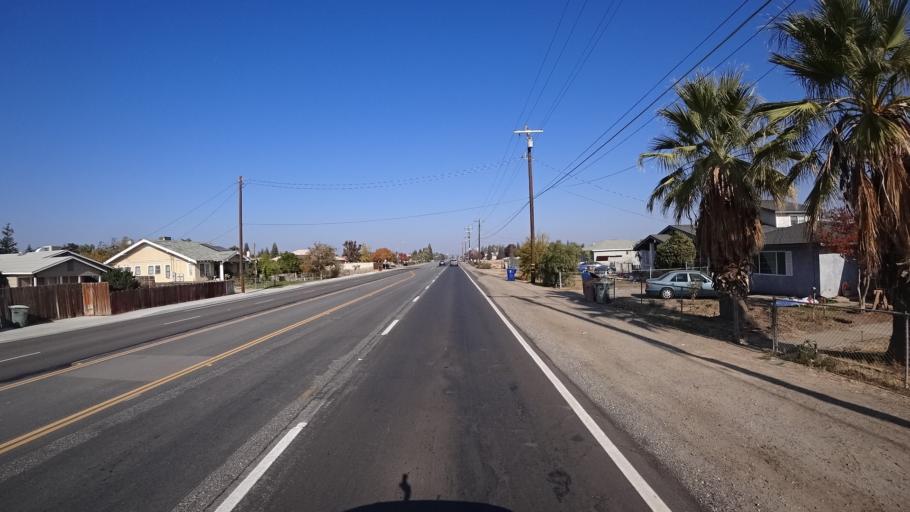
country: US
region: California
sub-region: Kern County
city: Greenfield
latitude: 35.2851
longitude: -119.0389
